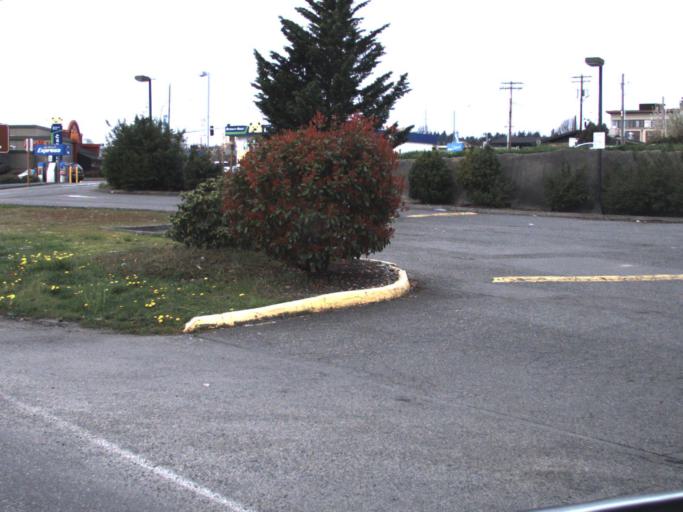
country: US
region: Washington
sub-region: King County
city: Des Moines
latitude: 47.3970
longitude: -122.3236
